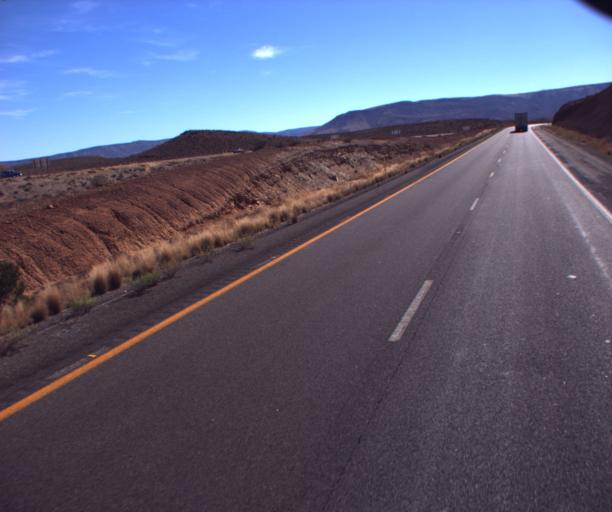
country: US
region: Utah
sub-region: Washington County
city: Saint George
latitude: 36.9970
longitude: -113.6247
